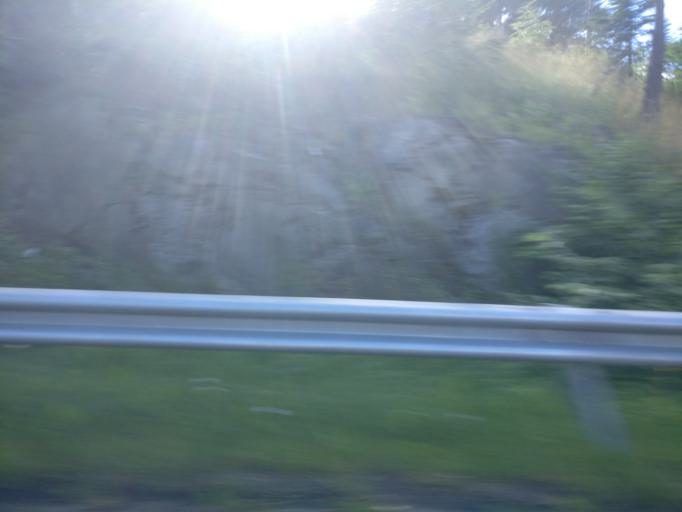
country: FI
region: Uusimaa
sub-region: Helsinki
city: Vihti
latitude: 60.4273
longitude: 24.4726
